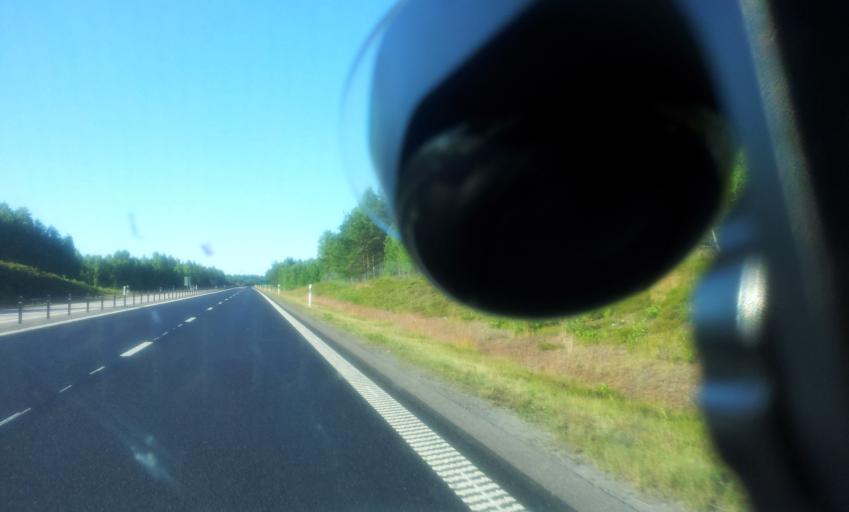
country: SE
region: Kalmar
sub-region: Torsas Kommun
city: Torsas
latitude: 56.5014
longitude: 16.0860
